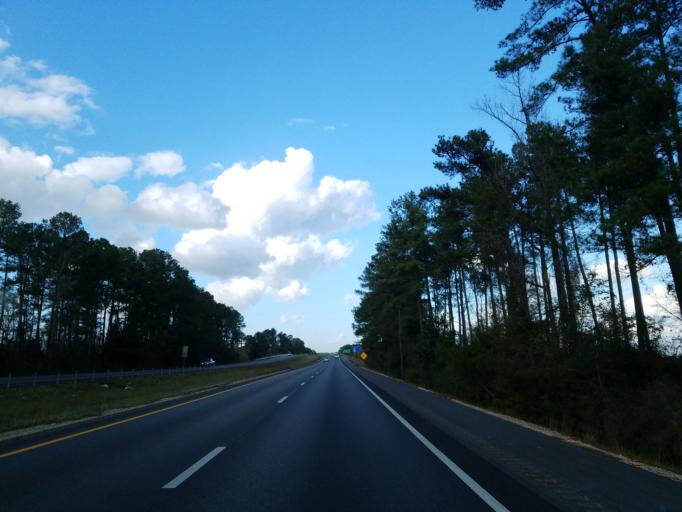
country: US
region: Mississippi
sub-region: Jones County
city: Laurel
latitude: 31.6556
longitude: -89.1614
